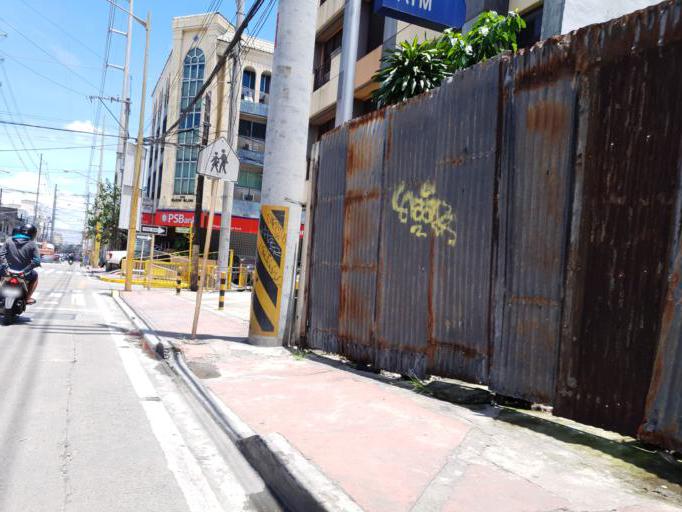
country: PH
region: Metro Manila
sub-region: Makati City
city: Makati City
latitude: 14.5682
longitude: 121.0137
